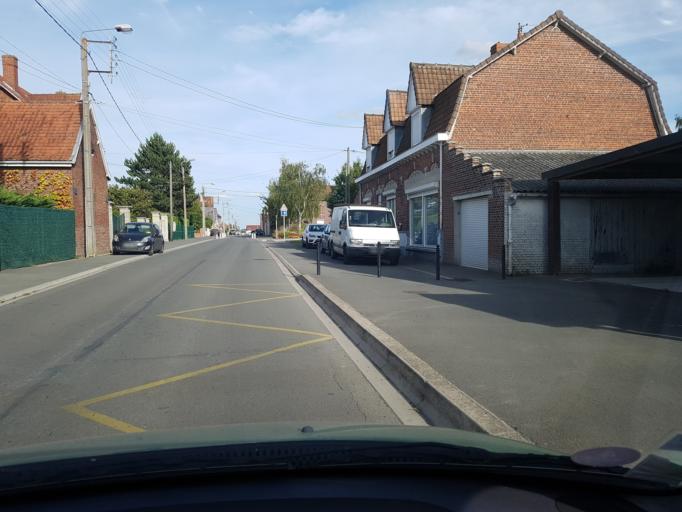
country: FR
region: Nord-Pas-de-Calais
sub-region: Departement du Pas-de-Calais
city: Lestrem
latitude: 50.6059
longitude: 2.6972
